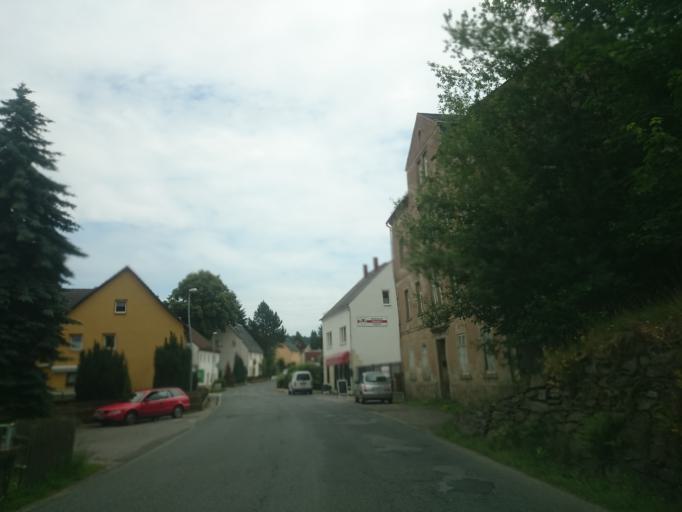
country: DE
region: Saxony
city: Grunhainichen
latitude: 50.7703
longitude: 13.1828
